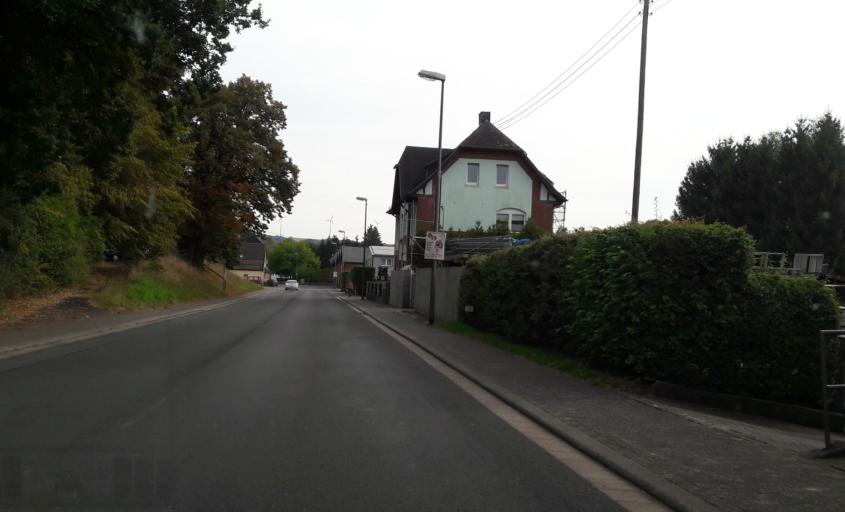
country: DE
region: Rheinland-Pfalz
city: Ellweiler
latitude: 49.6066
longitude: 7.1725
